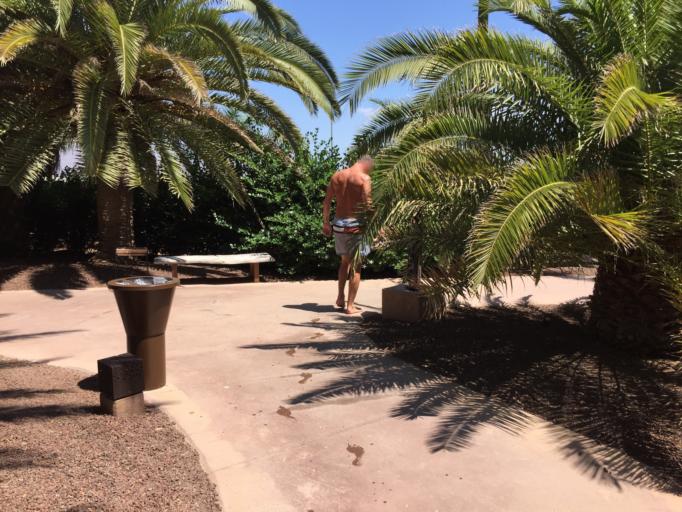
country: ES
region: Canary Islands
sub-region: Provincia de Las Palmas
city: Maspalomas
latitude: 27.7423
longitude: -15.5994
